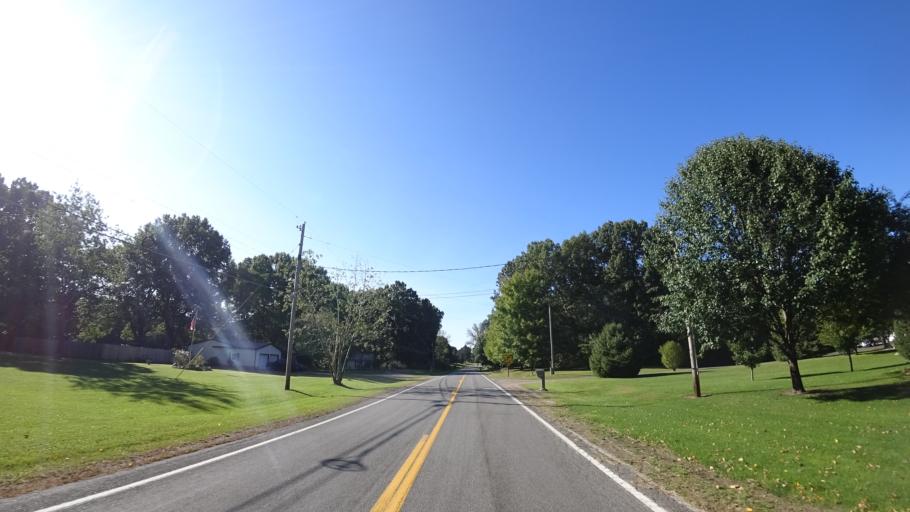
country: US
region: Michigan
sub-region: Berrien County
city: Lake Michigan Beach
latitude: 42.1774
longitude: -86.3848
